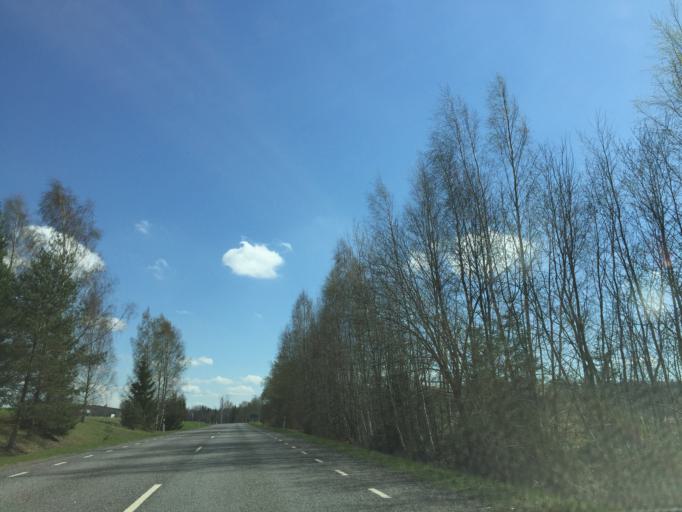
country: EE
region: Tartu
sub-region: Elva linn
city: Elva
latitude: 58.1499
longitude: 26.2266
